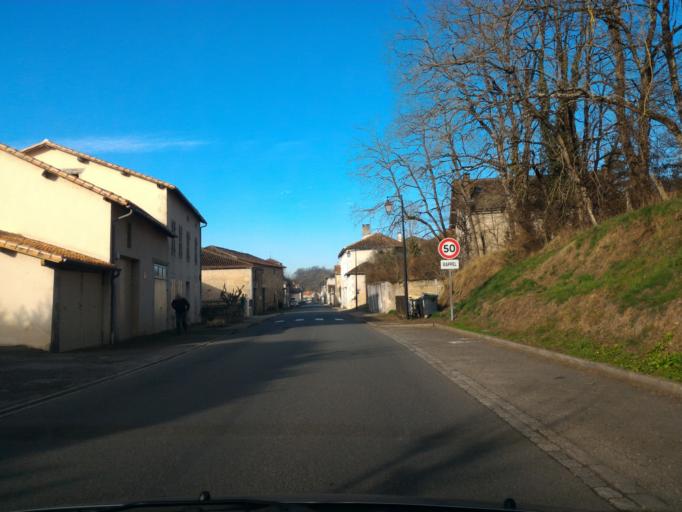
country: FR
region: Poitou-Charentes
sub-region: Departement de la Charente
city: Champagne-Mouton
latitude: 46.0247
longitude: 0.5196
